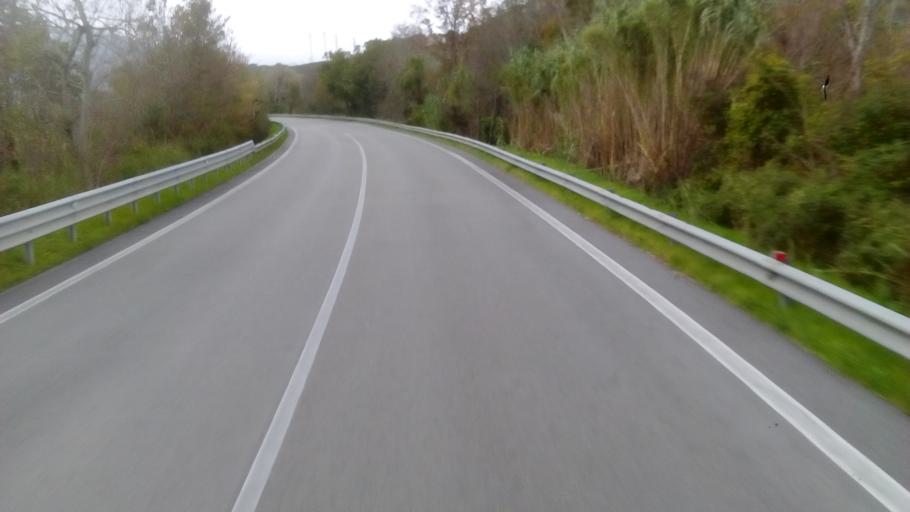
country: IT
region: Abruzzo
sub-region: Provincia di Chieti
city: Celenza sul Trigno
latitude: 41.8855
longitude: 14.6073
